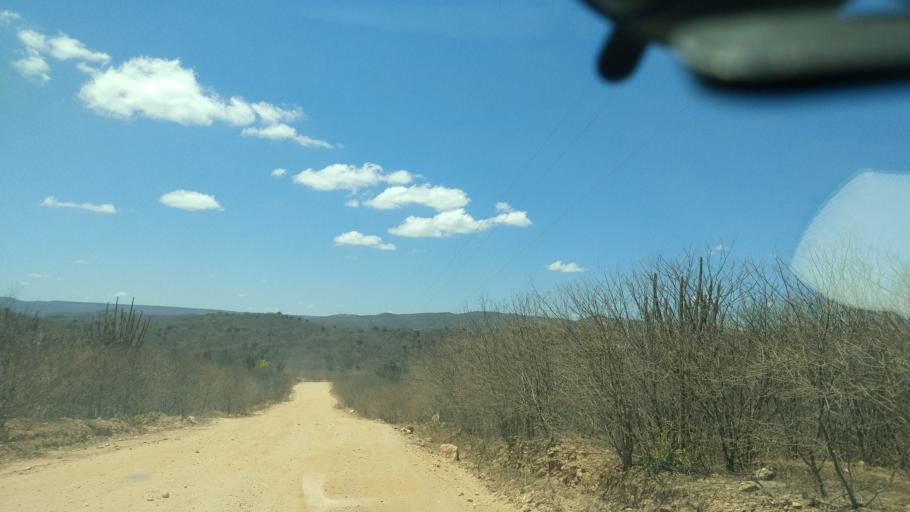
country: BR
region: Rio Grande do Norte
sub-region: Cerro Cora
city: Cerro Cora
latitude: -6.0095
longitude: -36.2871
